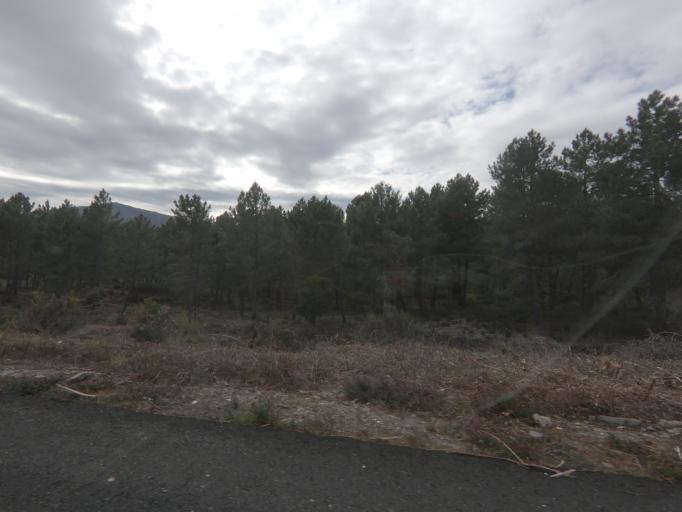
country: ES
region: Castille and Leon
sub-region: Provincia de Salamanca
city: Penaparda
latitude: 40.2598
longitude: -6.6895
